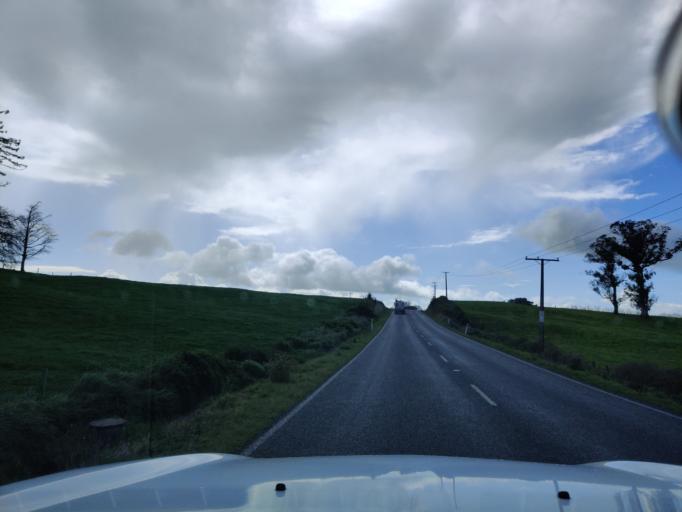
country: NZ
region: Waikato
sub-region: Waikato District
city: Ngaruawahia
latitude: -37.5748
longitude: 175.2406
